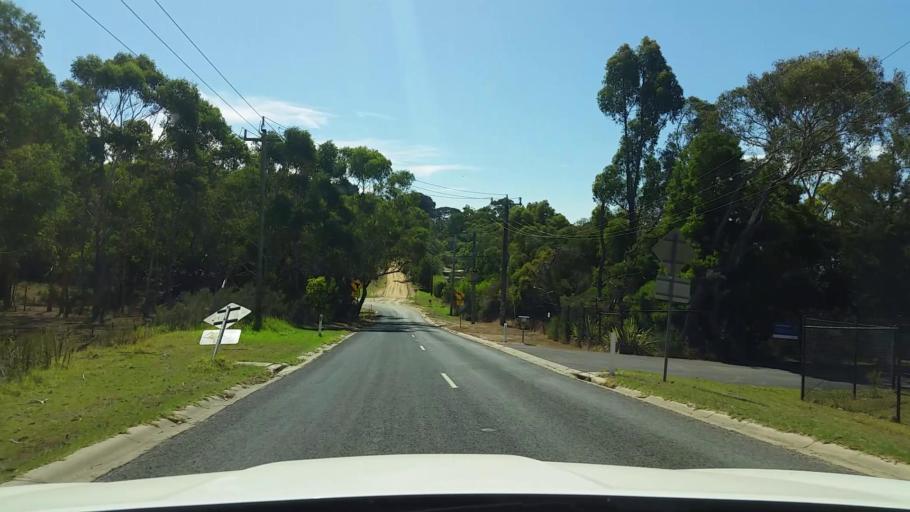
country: AU
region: Victoria
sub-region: Mornington Peninsula
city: Moorooduc
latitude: -38.2770
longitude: 145.0981
